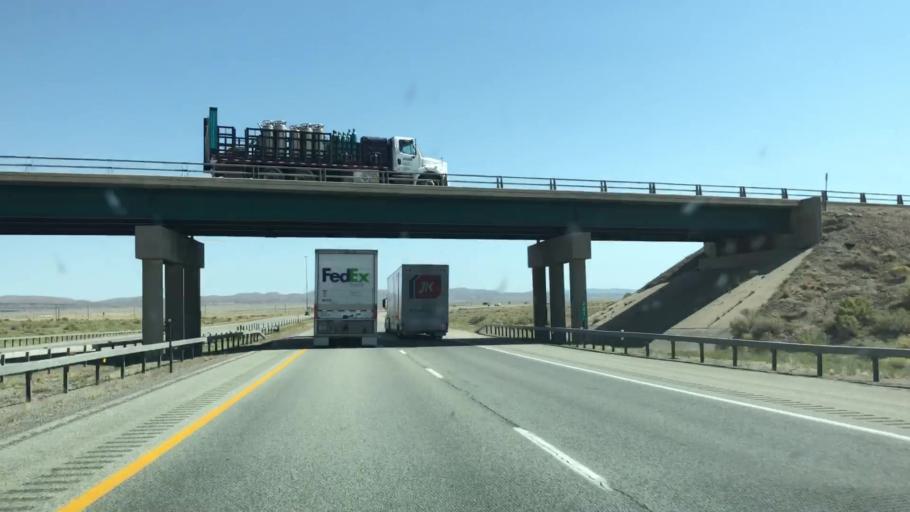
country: US
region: Wyoming
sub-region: Carbon County
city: Rawlins
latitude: 41.7720
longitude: -107.0783
